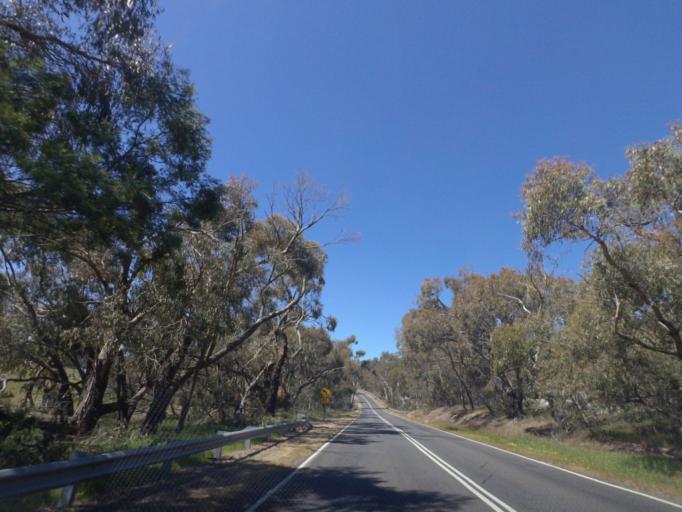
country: AU
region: Victoria
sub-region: Hume
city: Sunbury
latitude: -37.0717
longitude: 144.7751
